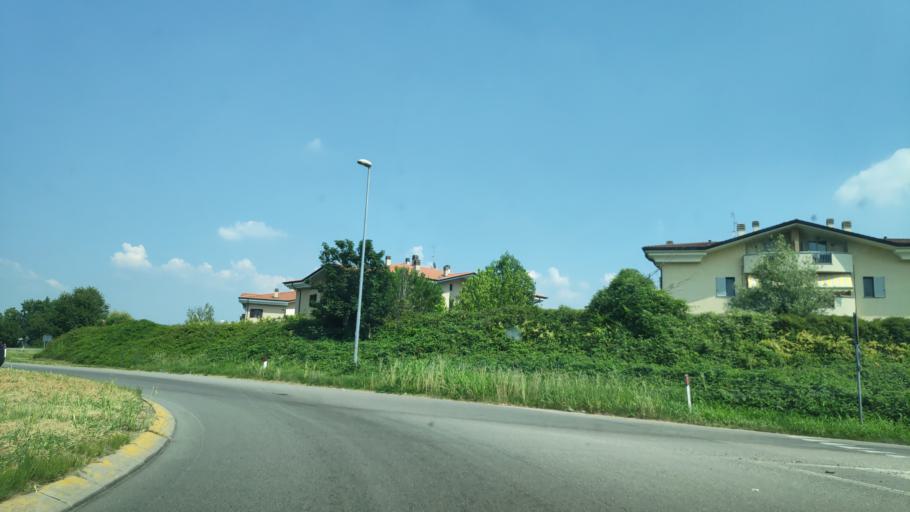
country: IT
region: Lombardy
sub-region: Citta metropolitana di Milano
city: Liscate
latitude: 45.4835
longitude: 9.4040
